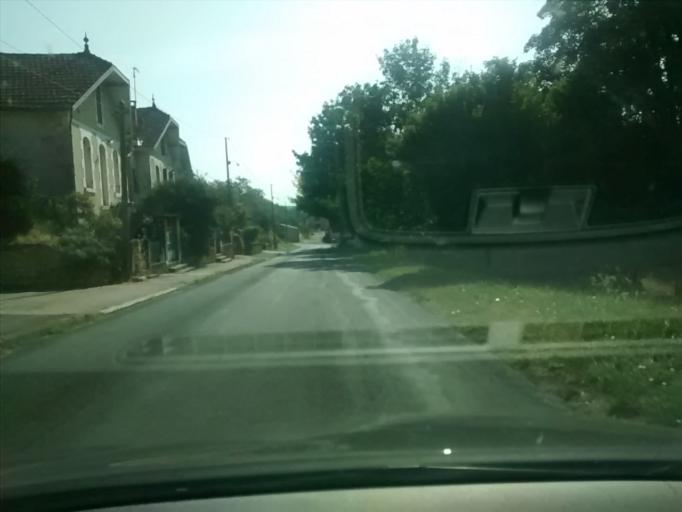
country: FR
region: Aquitaine
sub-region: Departement de la Dordogne
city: Lalinde
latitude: 44.8400
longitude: 0.7393
